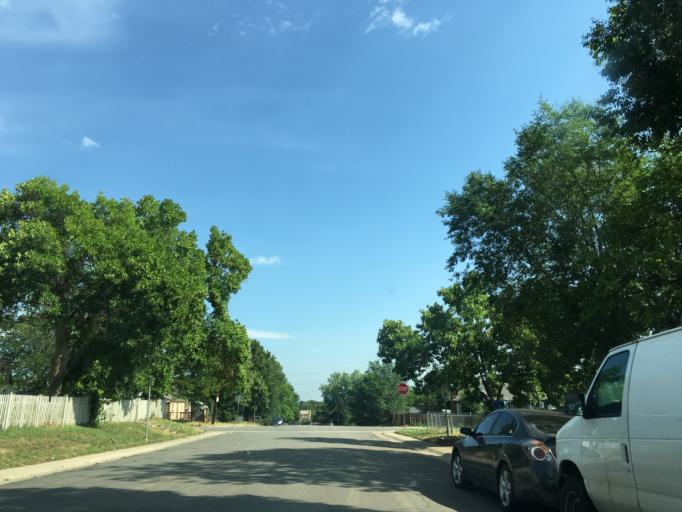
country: US
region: Colorado
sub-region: Jefferson County
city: Lakewood
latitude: 39.6980
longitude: -105.0402
